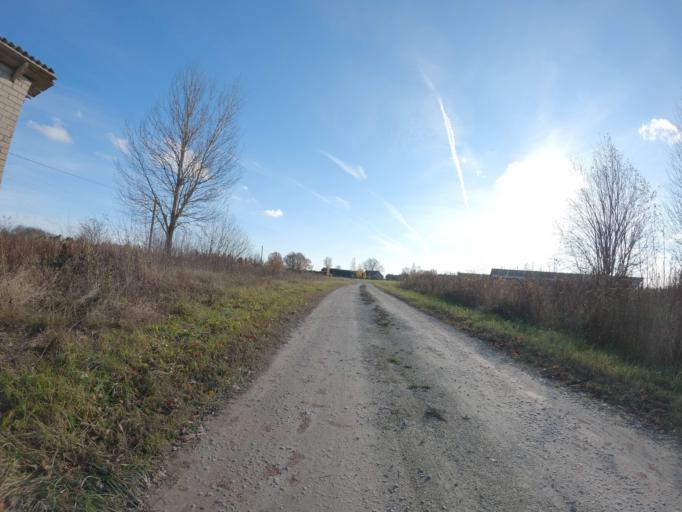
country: EE
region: Raplamaa
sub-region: Rapla vald
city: Rapla
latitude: 59.0269
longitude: 24.7942
